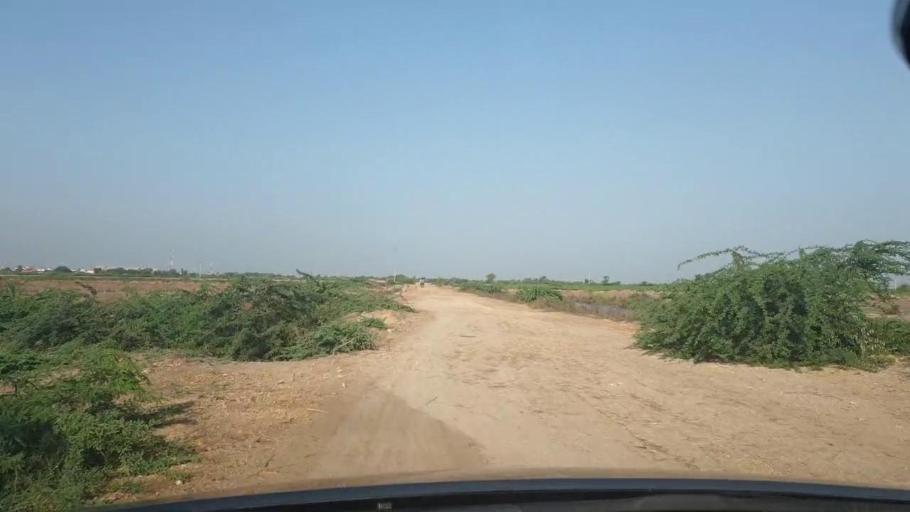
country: PK
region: Sindh
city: Tando Bago
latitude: 24.6452
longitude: 69.1309
